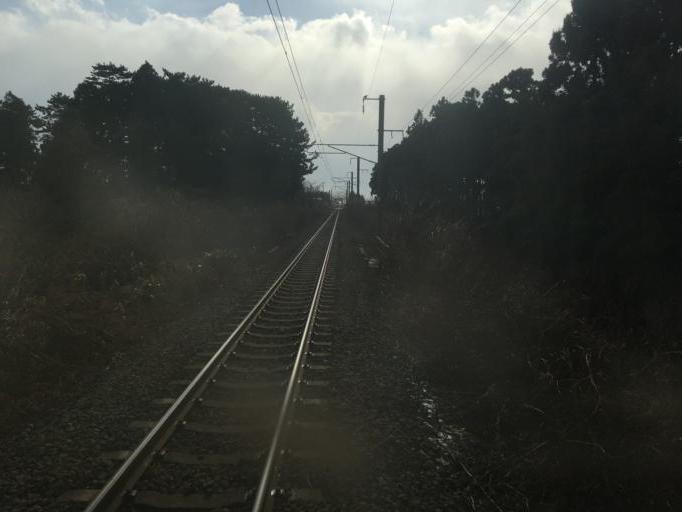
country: JP
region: Aomori
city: Aomori Shi
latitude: 40.9563
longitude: 140.6554
